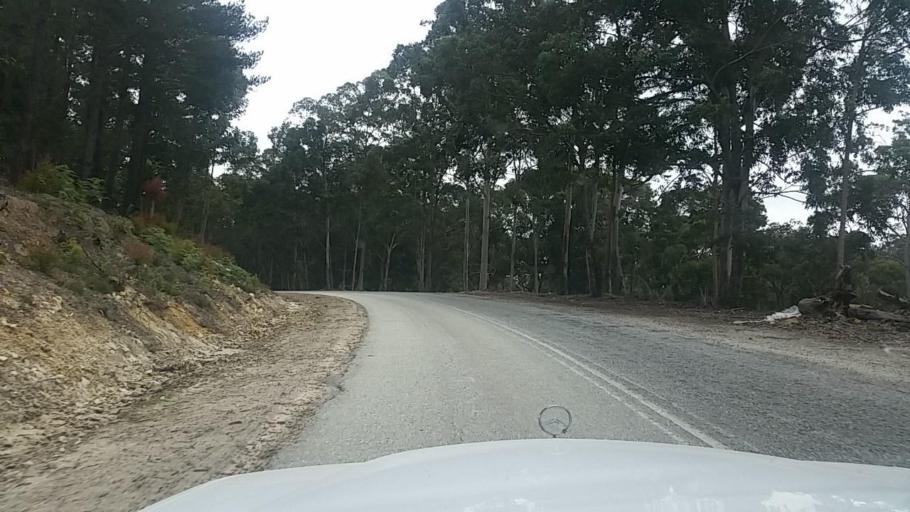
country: ZA
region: Western Cape
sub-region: Eden District Municipality
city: Knysna
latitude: -34.0063
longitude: 23.1154
